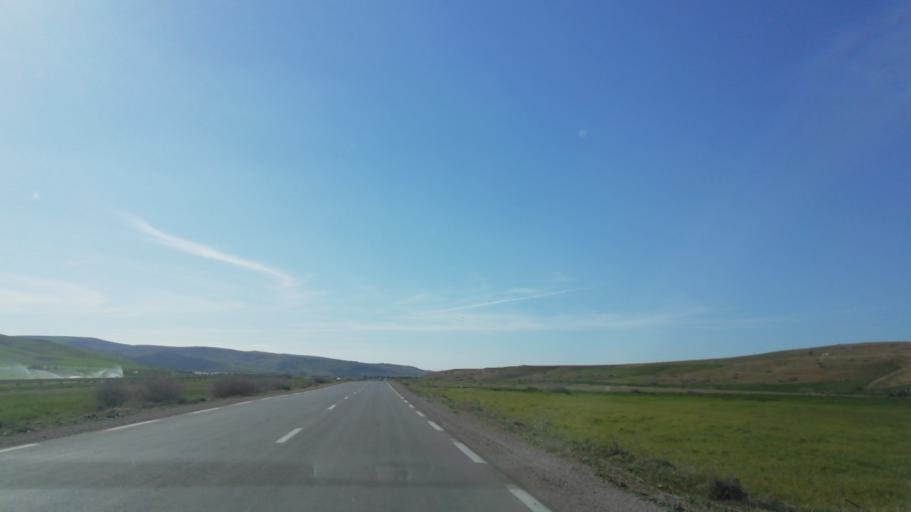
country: DZ
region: Mascara
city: Oued el Abtal
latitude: 35.4498
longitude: 0.8012
